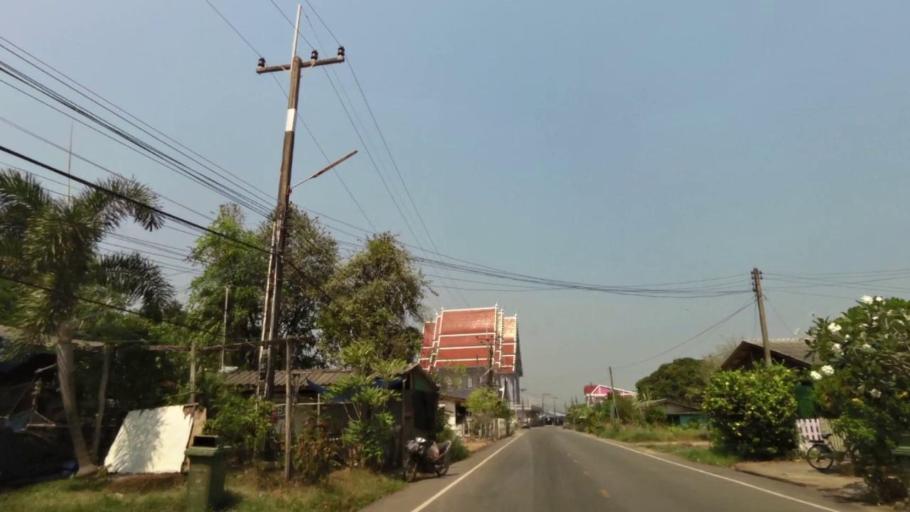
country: TH
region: Chanthaburi
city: Tha Mai
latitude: 12.5409
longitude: 101.9518
